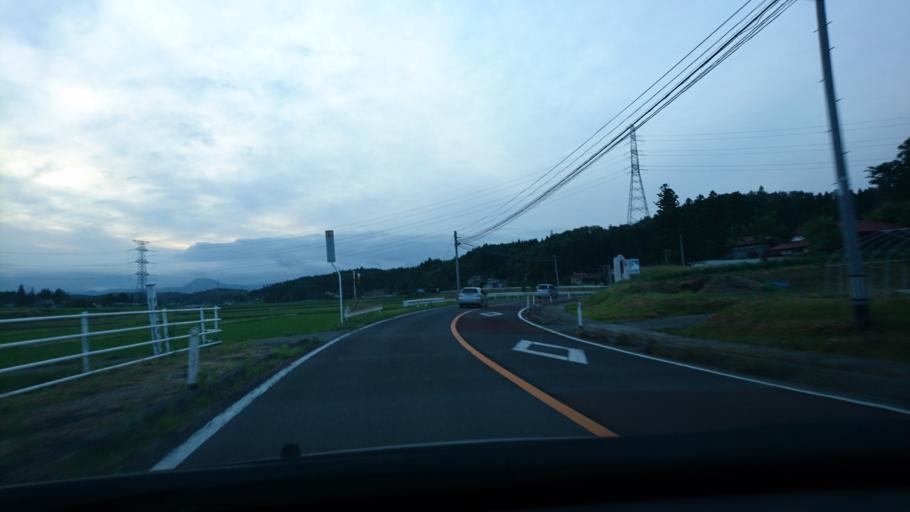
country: JP
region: Iwate
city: Ichinoseki
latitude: 38.7844
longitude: 140.9878
